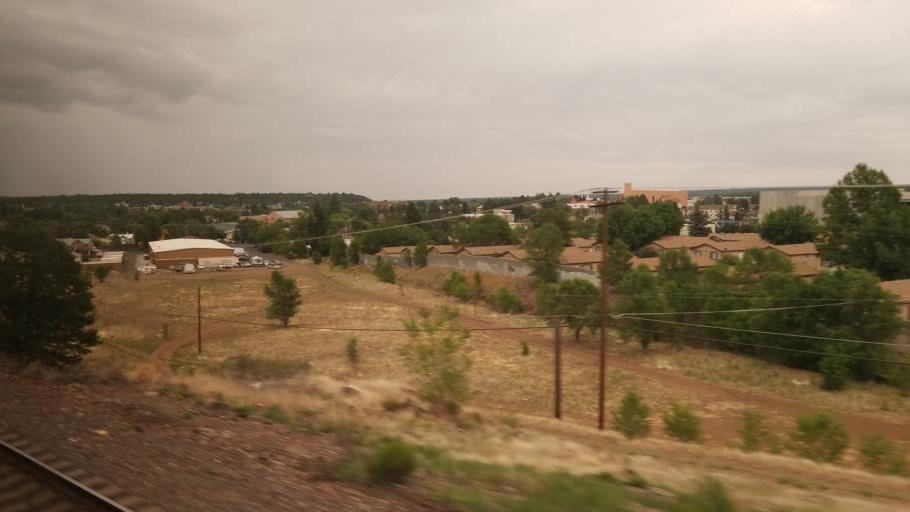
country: US
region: Arizona
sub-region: Coconino County
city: Flagstaff
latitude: 35.1944
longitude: -111.6649
